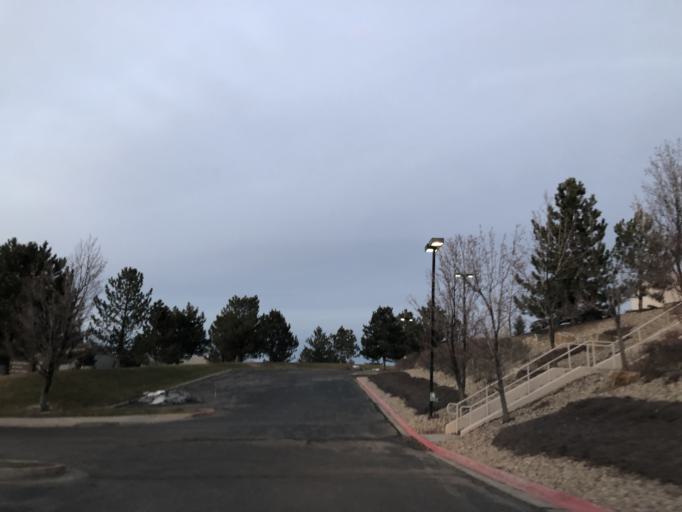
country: US
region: Colorado
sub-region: Douglas County
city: Meridian
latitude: 39.5588
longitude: -104.8591
